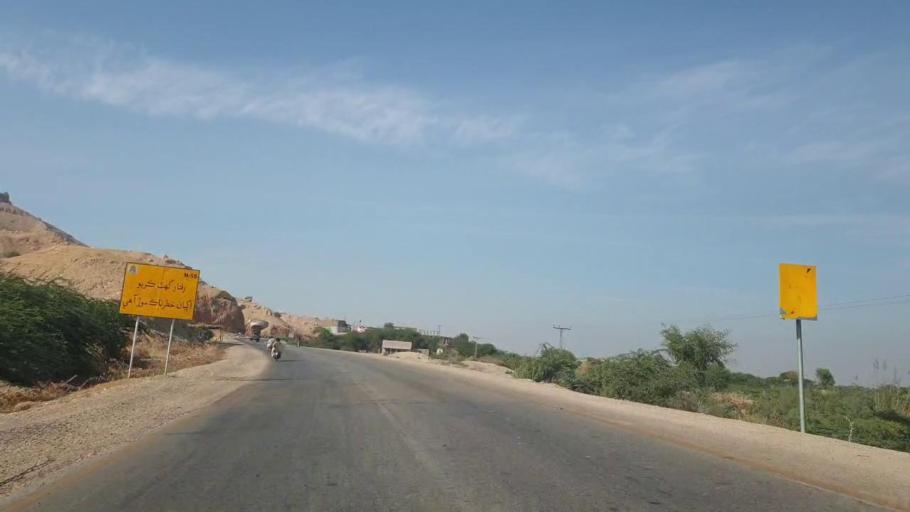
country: PK
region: Sindh
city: Sehwan
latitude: 26.3143
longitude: 67.8910
